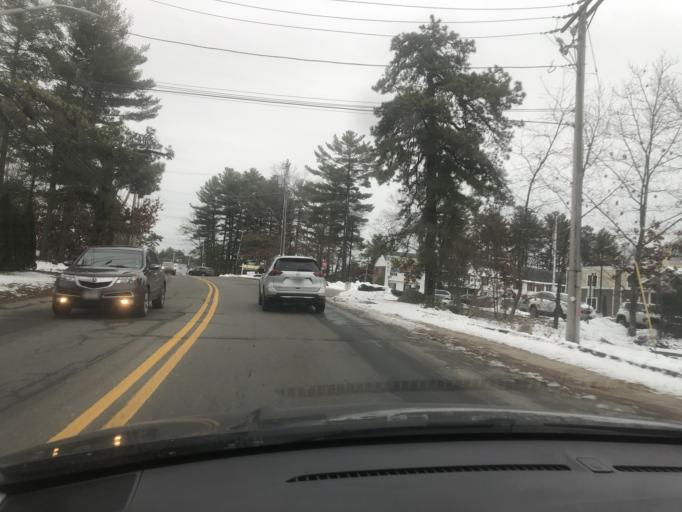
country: US
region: Massachusetts
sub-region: Middlesex County
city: Tewksbury
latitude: 42.5993
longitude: -71.2210
